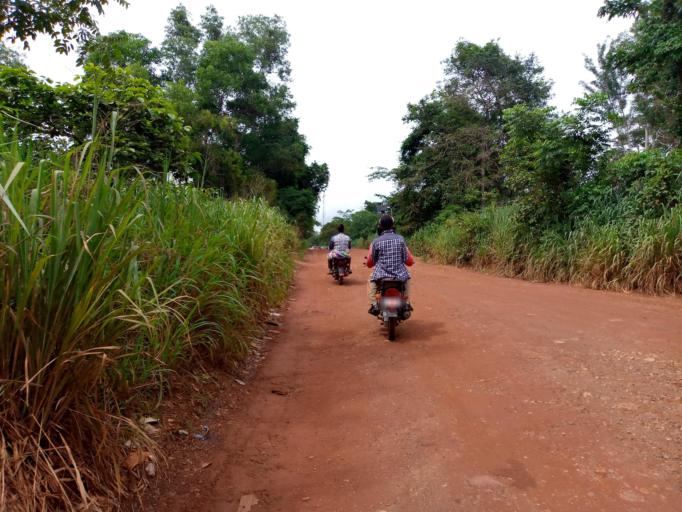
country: SL
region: Southern Province
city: Mogbwemo
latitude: 7.7700
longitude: -12.2962
